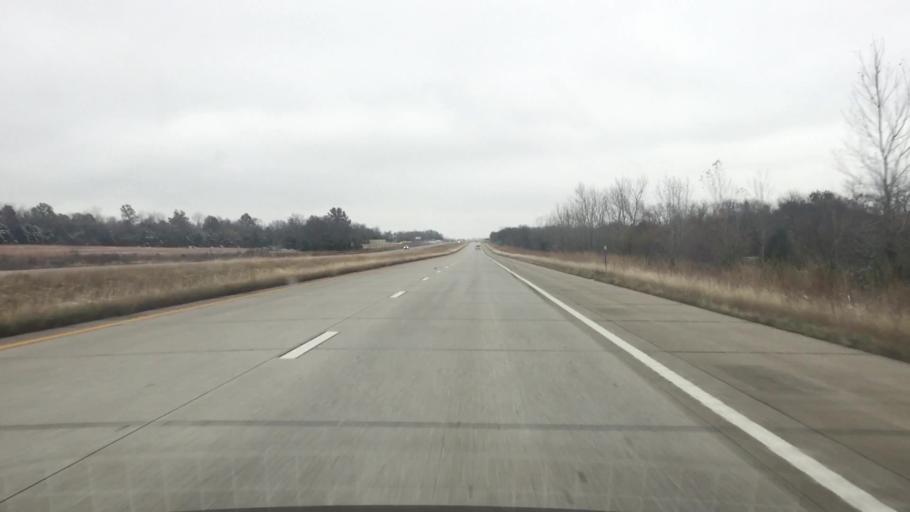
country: US
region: Missouri
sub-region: Henry County
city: Clinton
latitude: 38.2117
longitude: -93.7579
